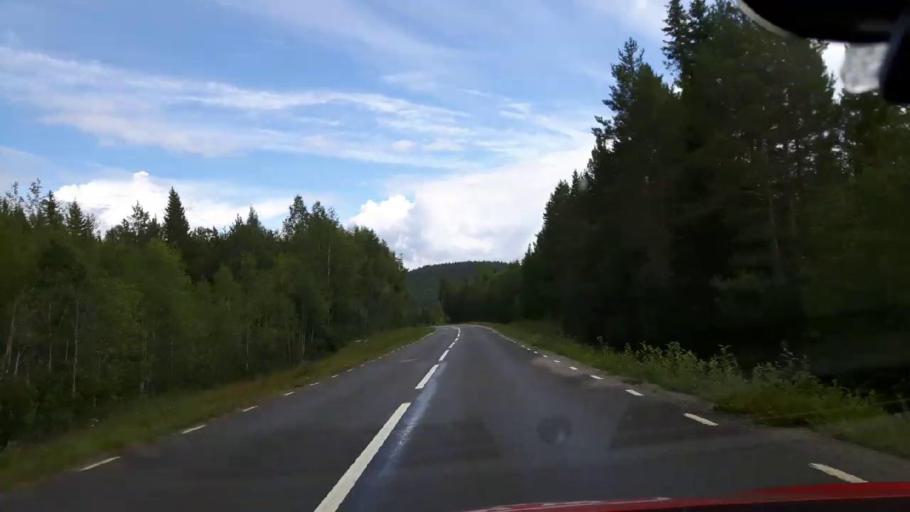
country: SE
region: Jaemtland
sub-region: Stroemsunds Kommun
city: Stroemsund
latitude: 64.3351
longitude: 14.9713
